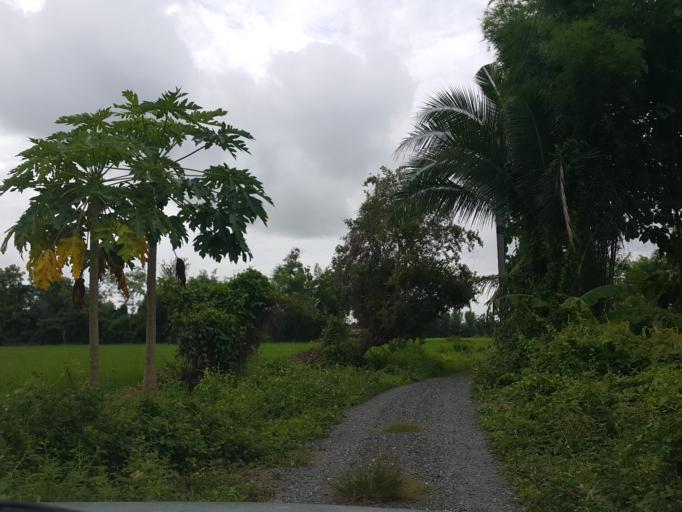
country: TH
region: Chiang Mai
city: San Sai
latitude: 18.8204
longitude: 99.1114
